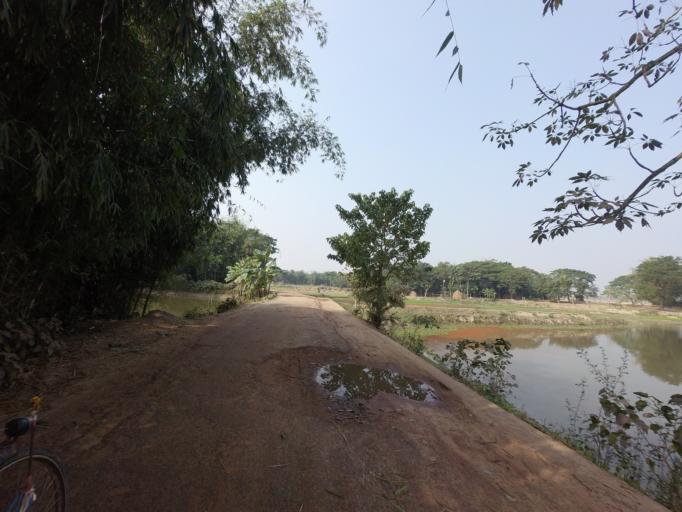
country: BD
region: Dhaka
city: Netrakona
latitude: 25.0139
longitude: 90.6927
